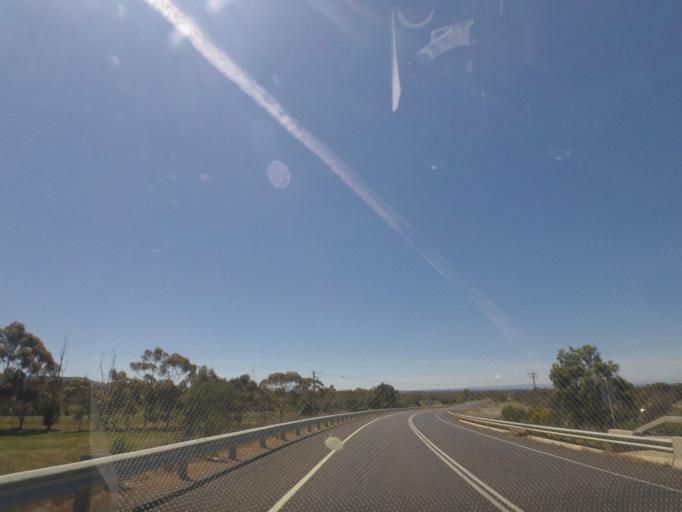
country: AU
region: Victoria
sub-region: Hume
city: Sunbury
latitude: -37.4683
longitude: 144.6518
